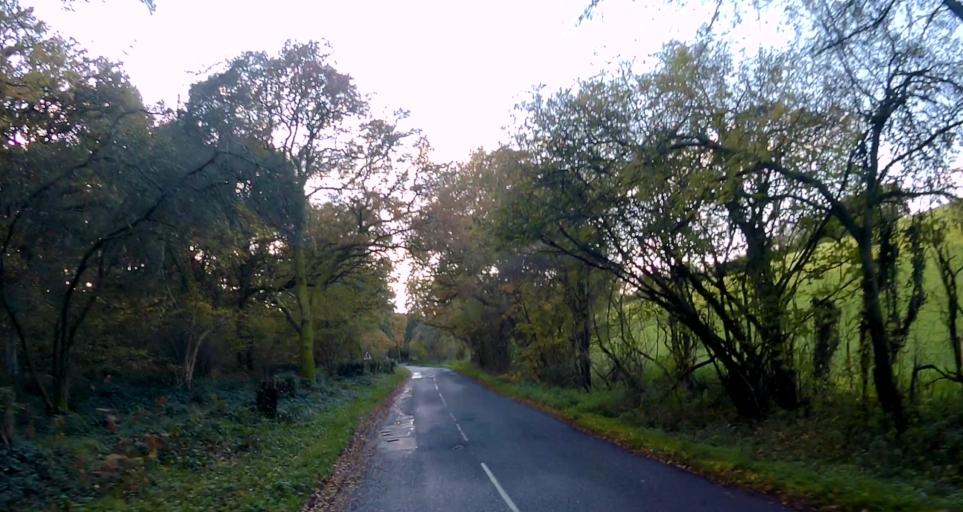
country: GB
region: England
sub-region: Hampshire
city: Basingstoke
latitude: 51.1915
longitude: -1.0860
